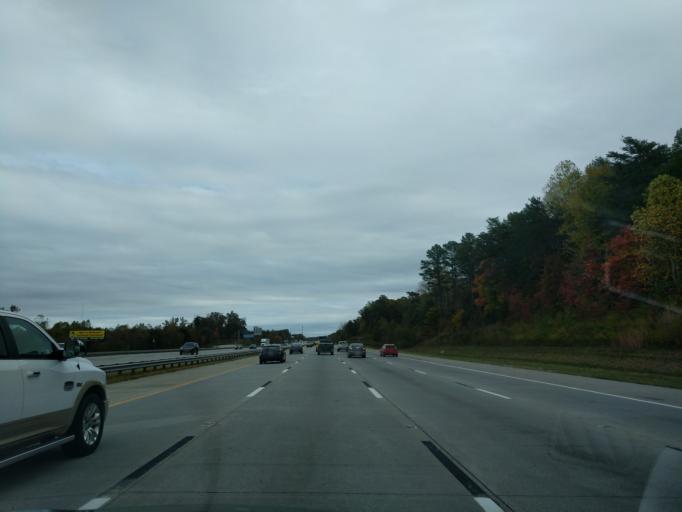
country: US
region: North Carolina
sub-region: Rowan County
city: East Spencer
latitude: 35.6655
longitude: -80.4436
